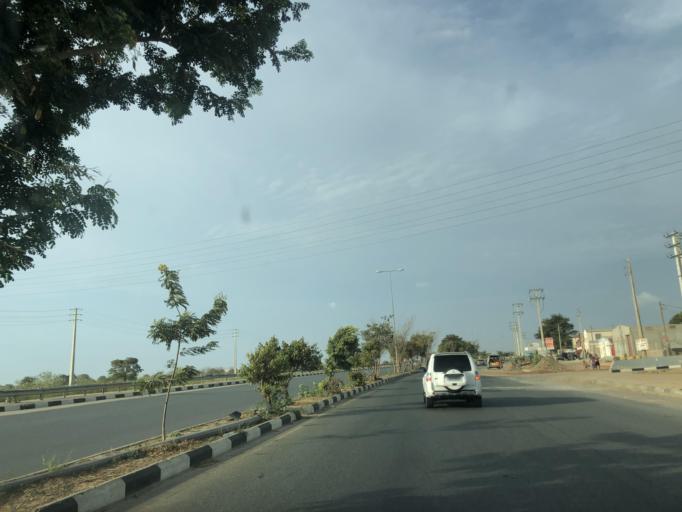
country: AO
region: Luanda
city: Luanda
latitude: -8.9395
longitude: 13.2953
